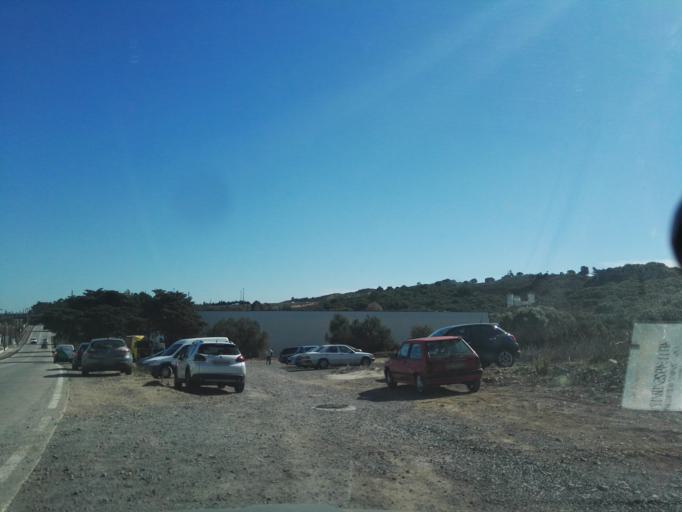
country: PT
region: Lisbon
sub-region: Sintra
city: Sintra
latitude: 38.8005
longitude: -9.3687
